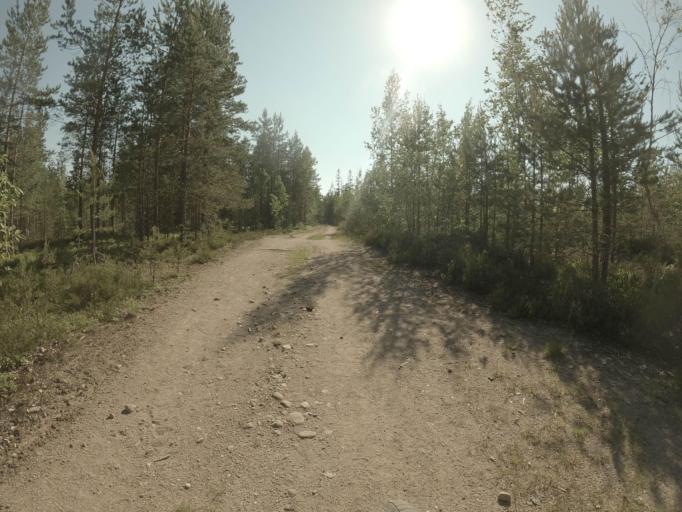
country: RU
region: Leningrad
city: Yakovlevo
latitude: 60.4548
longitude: 29.2645
